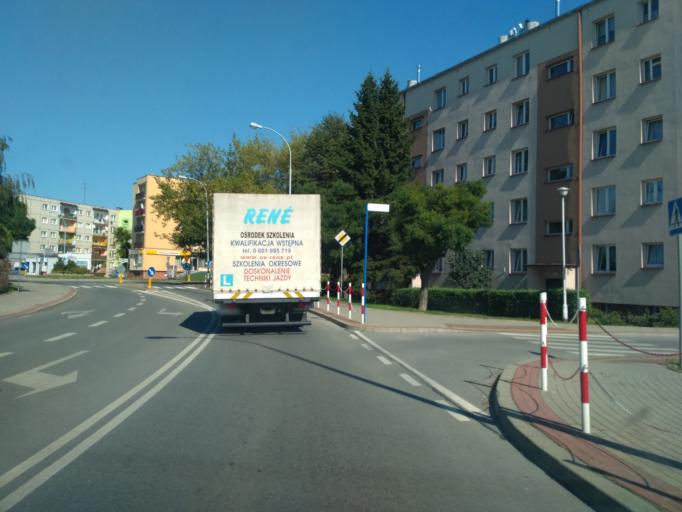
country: PL
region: Subcarpathian Voivodeship
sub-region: Krosno
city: Krosno
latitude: 49.6871
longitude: 21.7714
